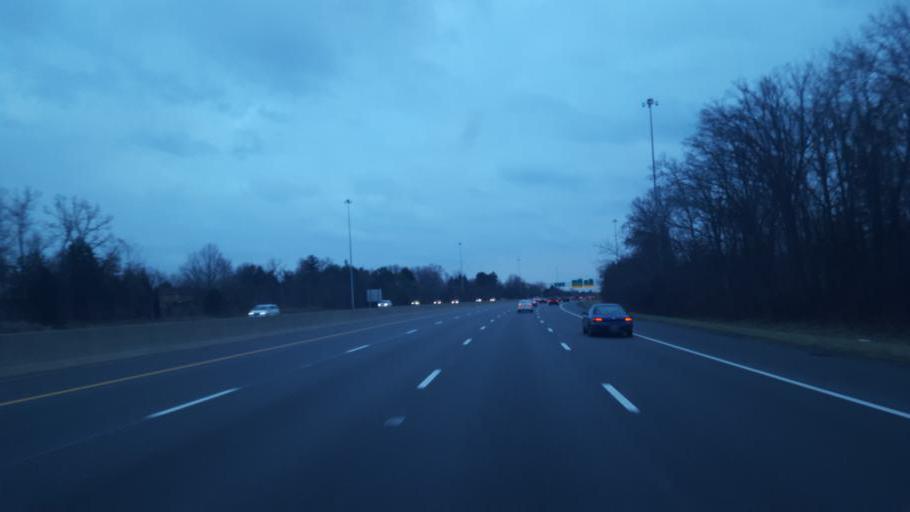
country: US
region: Ohio
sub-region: Franklin County
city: Reynoldsburg
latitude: 39.9654
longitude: -82.8433
